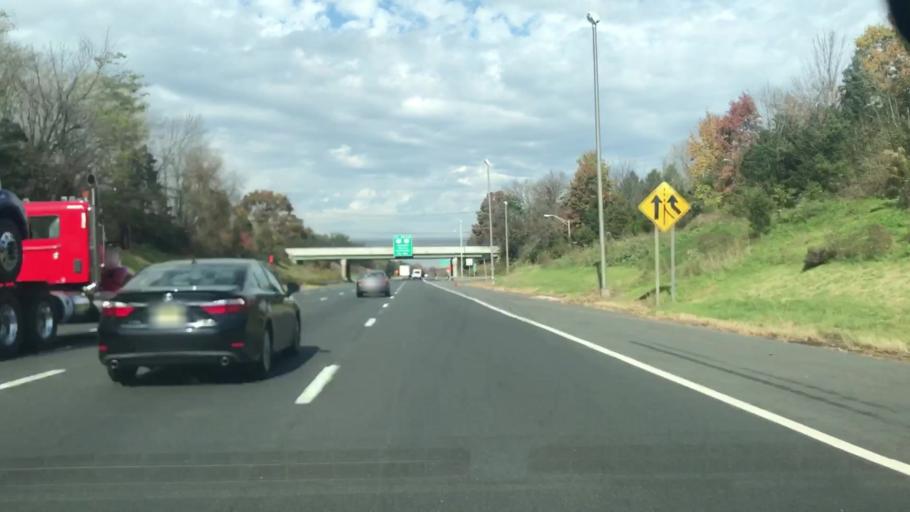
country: US
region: New Jersey
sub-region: Somerset County
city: Bedminster
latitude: 40.6450
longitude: -74.6454
